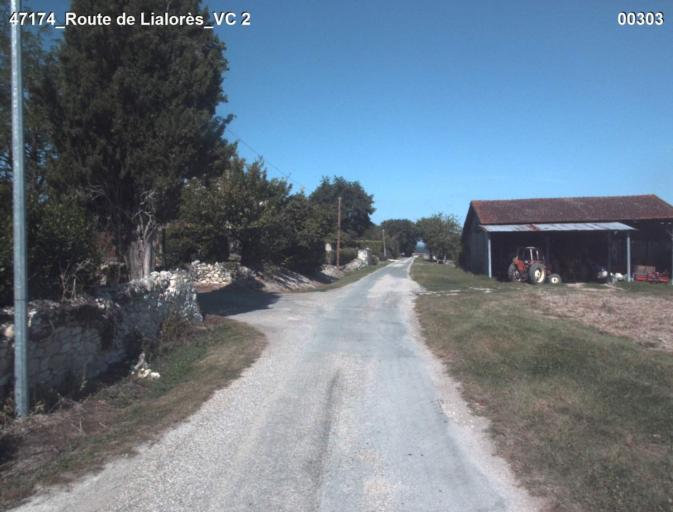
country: FR
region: Midi-Pyrenees
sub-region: Departement du Gers
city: Condom
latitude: 44.0101
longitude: 0.3812
